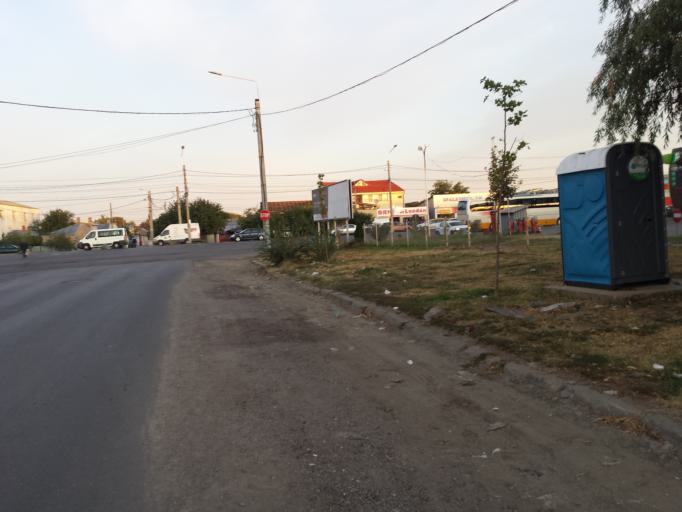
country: RO
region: Braila
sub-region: Municipiul Braila
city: Braila
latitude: 45.2387
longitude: 27.9441
